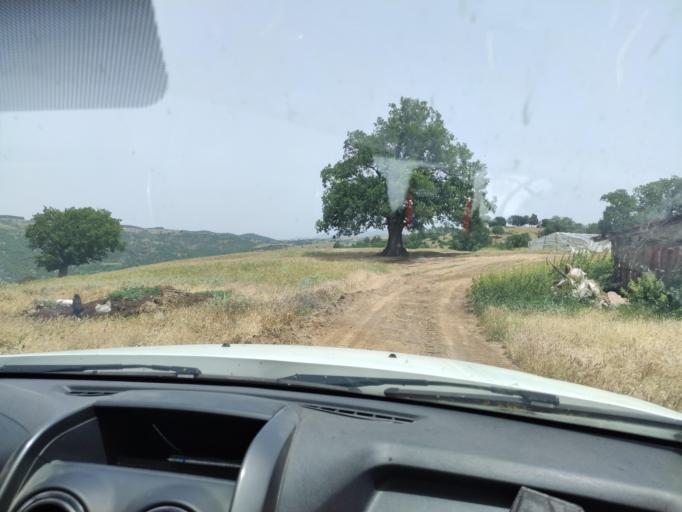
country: MK
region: Radovis
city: Radovish
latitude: 41.6781
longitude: 22.4004
